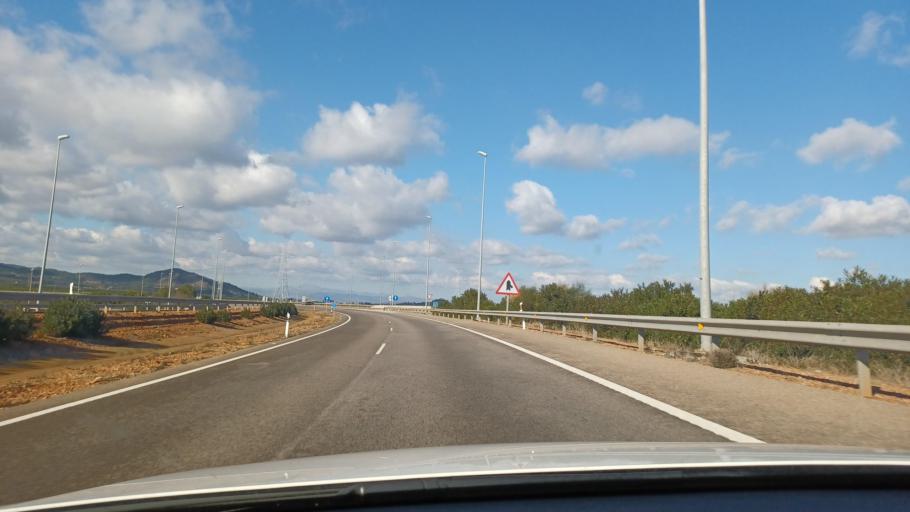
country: ES
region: Valencia
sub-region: Provincia de Castello
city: Nules
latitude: 39.8617
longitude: -0.1690
